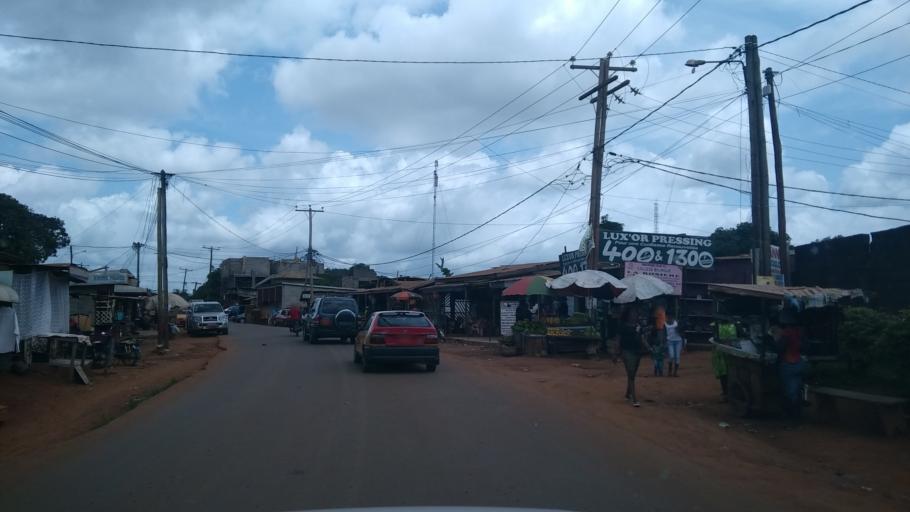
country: CM
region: Centre
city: Yaounde
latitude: 3.8128
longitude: 11.4893
